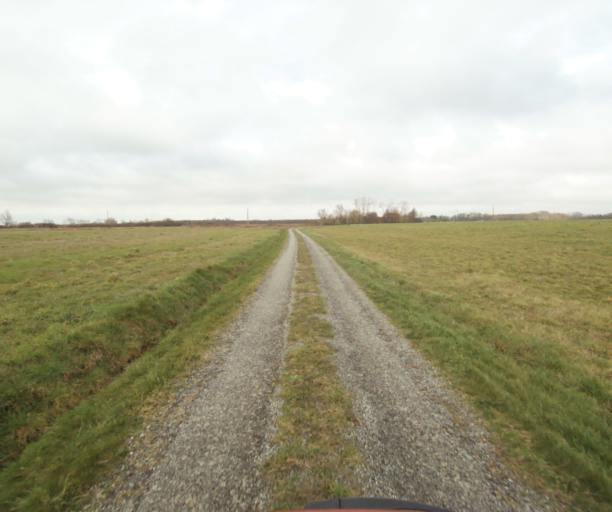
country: FR
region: Midi-Pyrenees
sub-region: Departement de l'Ariege
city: La Tour-du-Crieu
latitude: 43.1561
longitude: 1.6913
